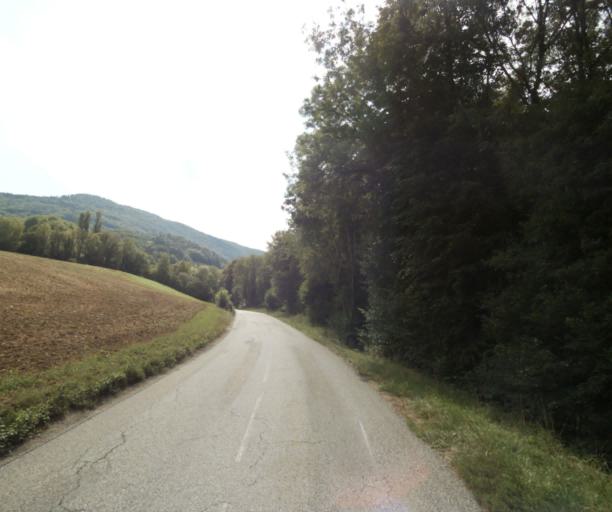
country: FR
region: Rhone-Alpes
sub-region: Departement de l'Isere
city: La Tronche
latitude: 45.2441
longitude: 5.7239
